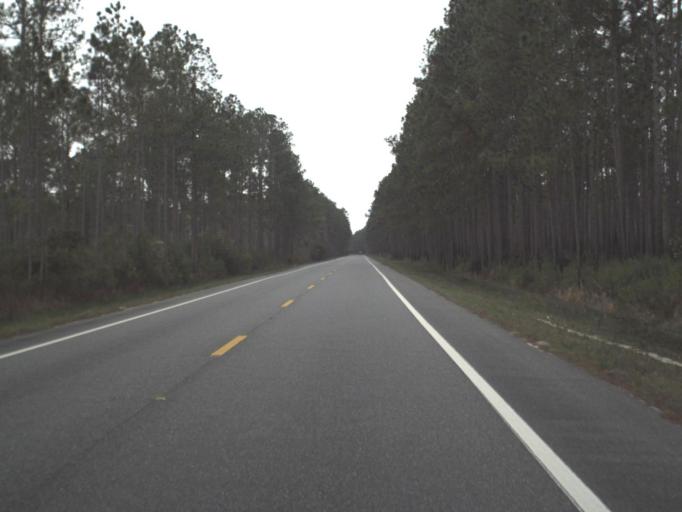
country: US
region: Florida
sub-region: Franklin County
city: Apalachicola
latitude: 29.9719
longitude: -84.9752
